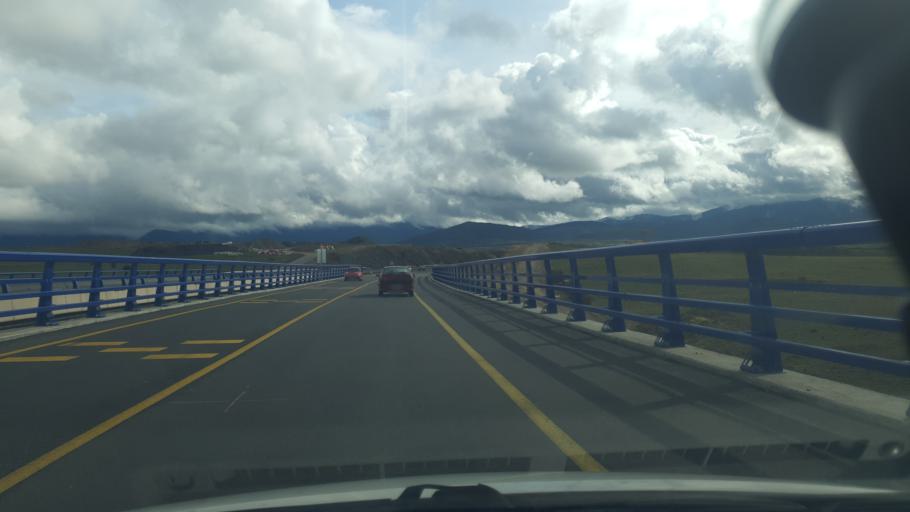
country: ES
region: Castille and Leon
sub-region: Provincia de Segovia
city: San Cristobal de Segovia
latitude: 40.9472
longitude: -4.0881
